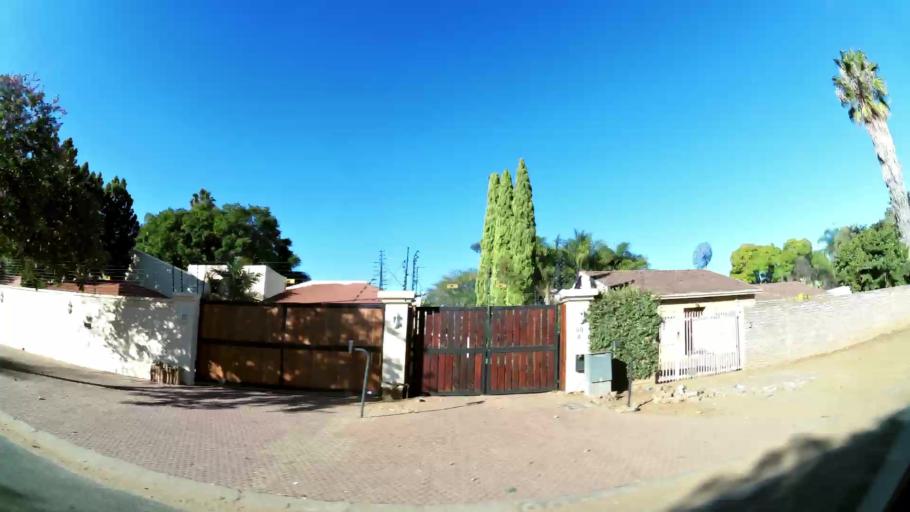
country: ZA
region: Limpopo
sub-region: Capricorn District Municipality
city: Polokwane
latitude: -23.9012
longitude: 29.4652
